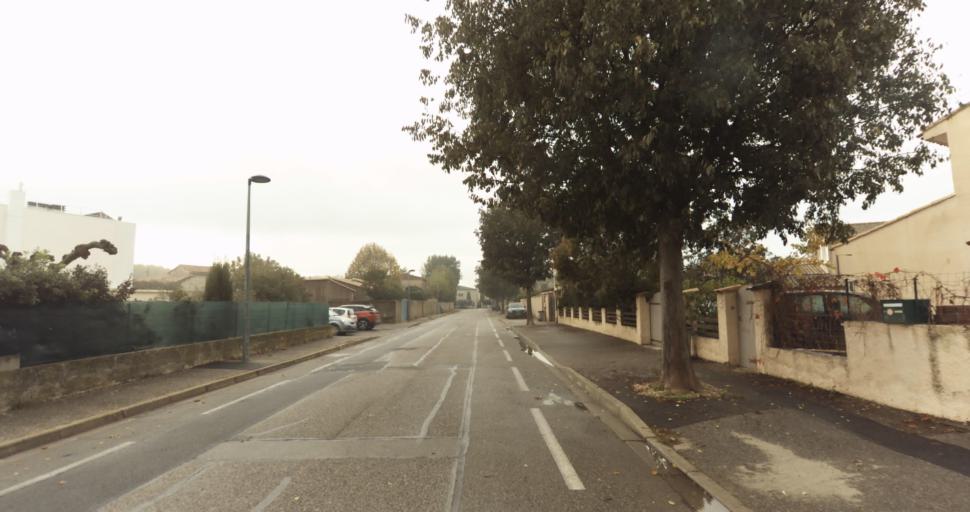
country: FR
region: Provence-Alpes-Cote d'Azur
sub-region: Departement des Bouches-du-Rhone
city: Rognonas
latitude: 43.9038
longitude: 4.8080
